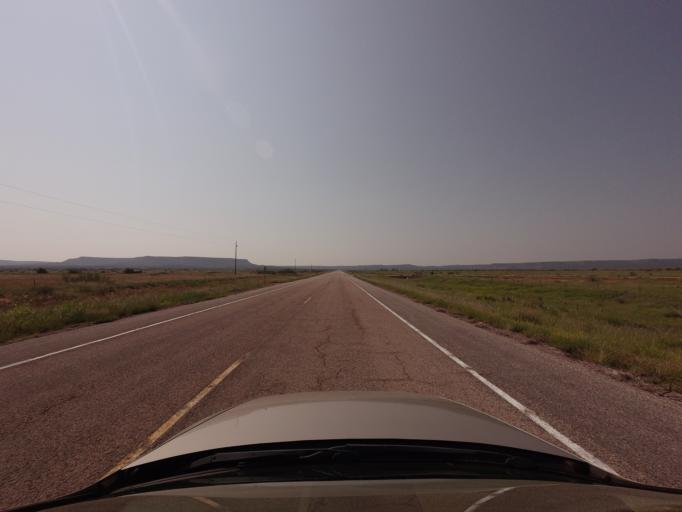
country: US
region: New Mexico
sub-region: Quay County
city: Tucumcari
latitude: 34.8663
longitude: -103.7604
